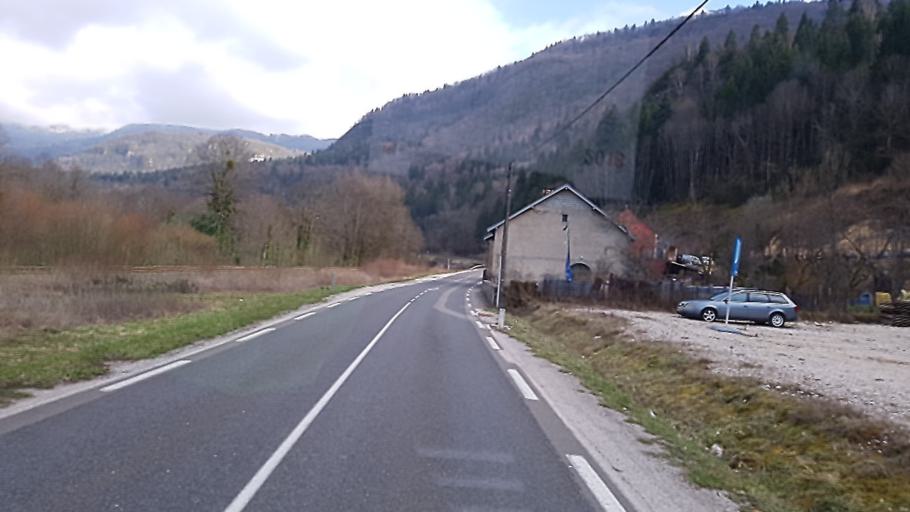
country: FR
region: Franche-Comte
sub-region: Departement du Jura
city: Lavans-les-Saint-Claude
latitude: 46.3515
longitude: 5.7461
